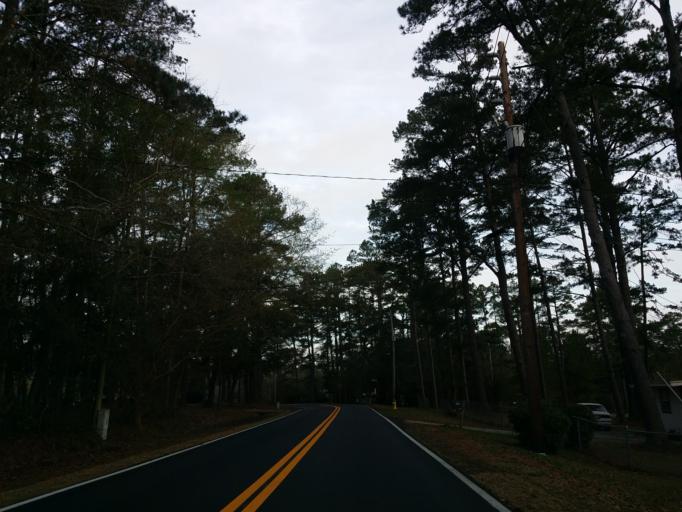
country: US
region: Florida
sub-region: Leon County
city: Tallahassee
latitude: 30.4722
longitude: -84.2157
